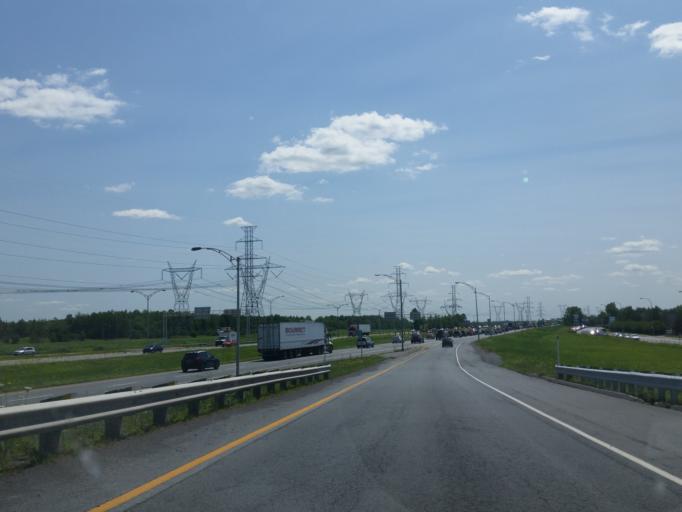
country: CA
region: Quebec
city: Saint-Bruno-de-Montarville
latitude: 45.4782
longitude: -73.3866
